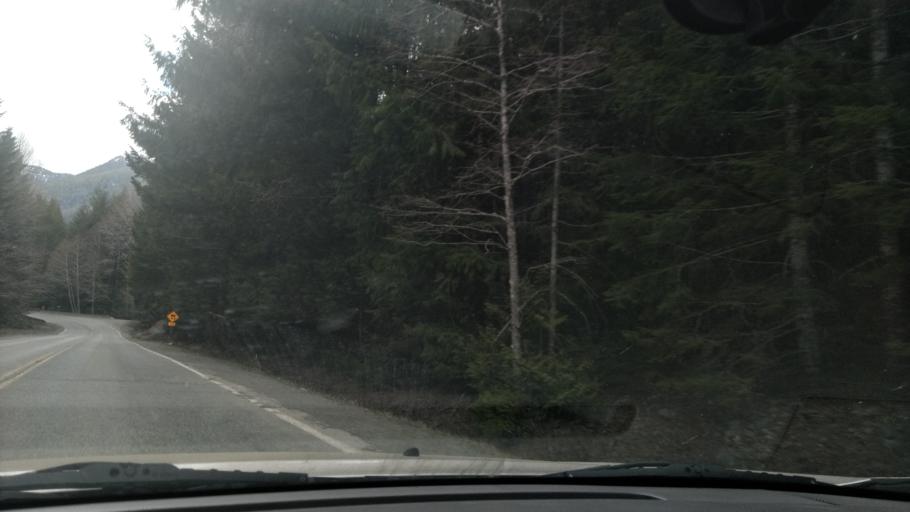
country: CA
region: British Columbia
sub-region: Regional District of Alberni-Clayoquot
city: Tofino
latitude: 49.8401
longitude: -125.9257
